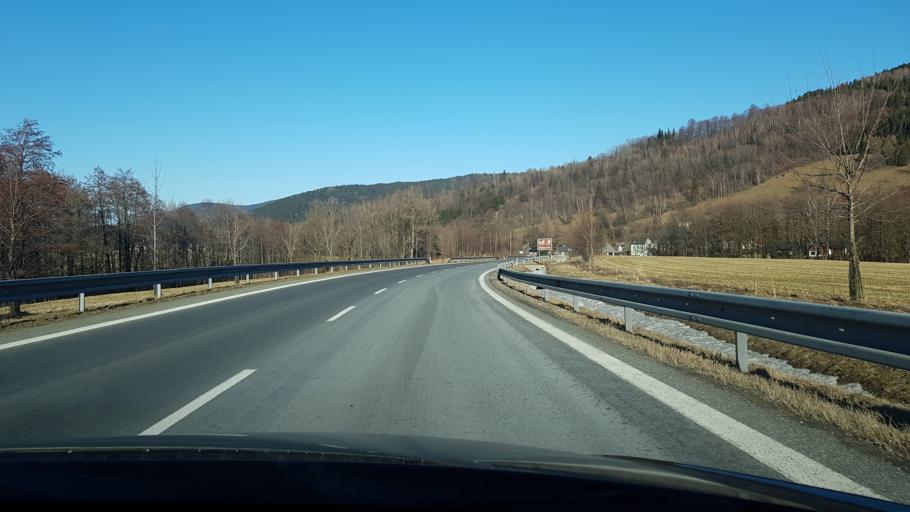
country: CZ
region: Olomoucky
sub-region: Okres Jesenik
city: Jesenik
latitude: 50.1585
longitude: 17.1902
